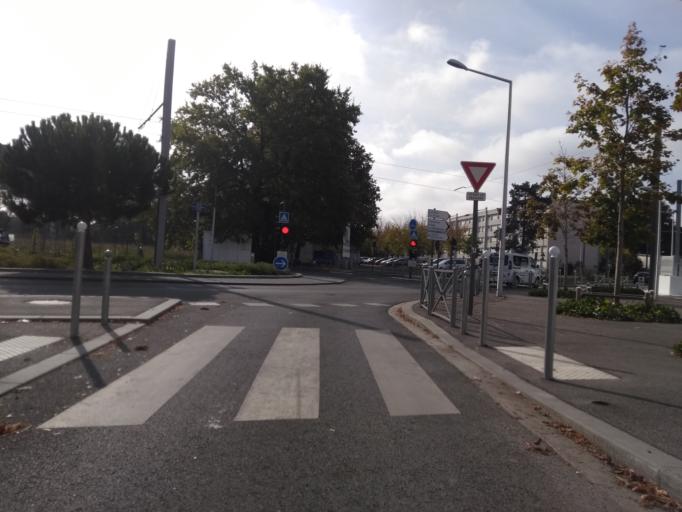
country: FR
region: Aquitaine
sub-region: Departement de la Gironde
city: Pessac
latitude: 44.7940
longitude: -0.6381
